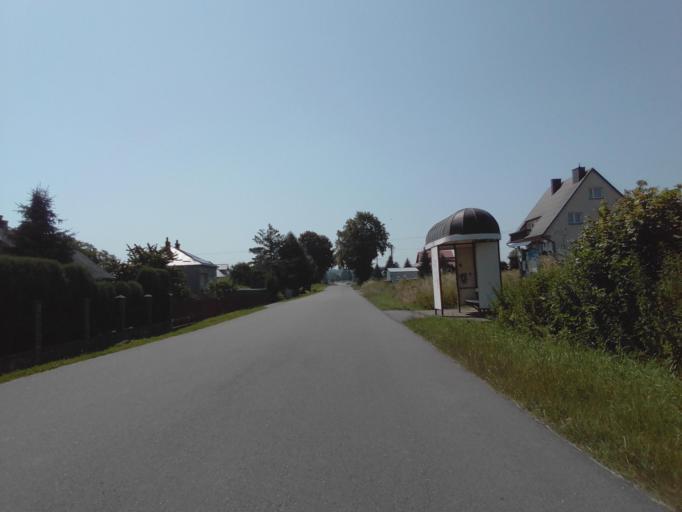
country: PL
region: Subcarpathian Voivodeship
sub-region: Powiat ropczycko-sedziszowski
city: Sedziszow Malopolski
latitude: 50.0642
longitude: 21.6637
